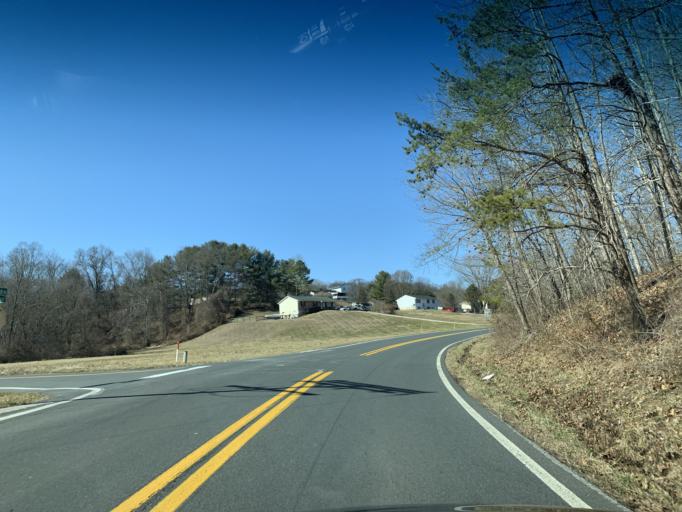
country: US
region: Maryland
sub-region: Carroll County
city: Hampstead
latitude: 39.5754
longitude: -76.8967
